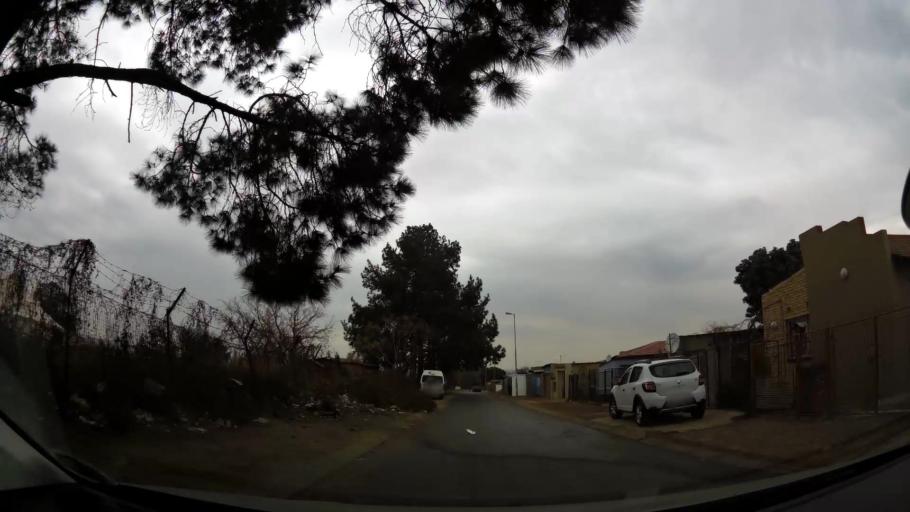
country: ZA
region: Gauteng
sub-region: City of Johannesburg Metropolitan Municipality
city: Soweto
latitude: -26.2519
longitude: 27.8733
